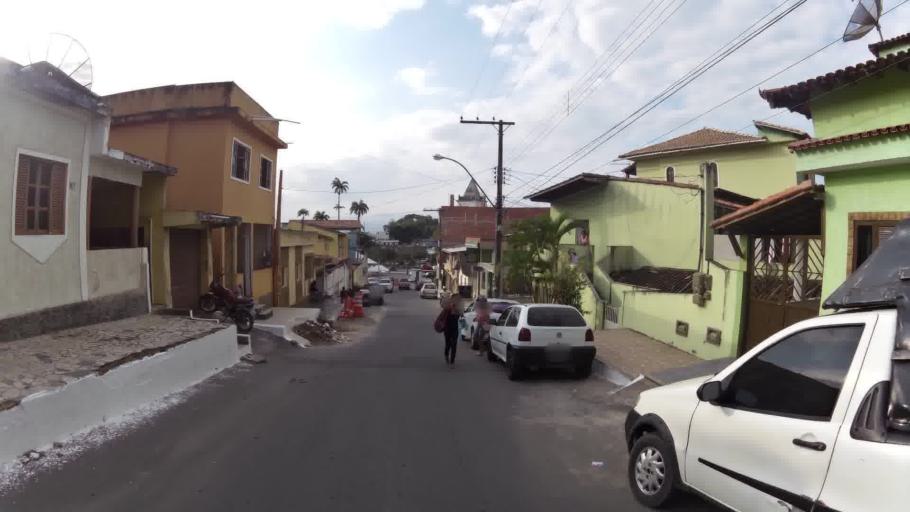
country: BR
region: Espirito Santo
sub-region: Itapemirim
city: Itapemirim
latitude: -21.0113
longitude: -40.8329
